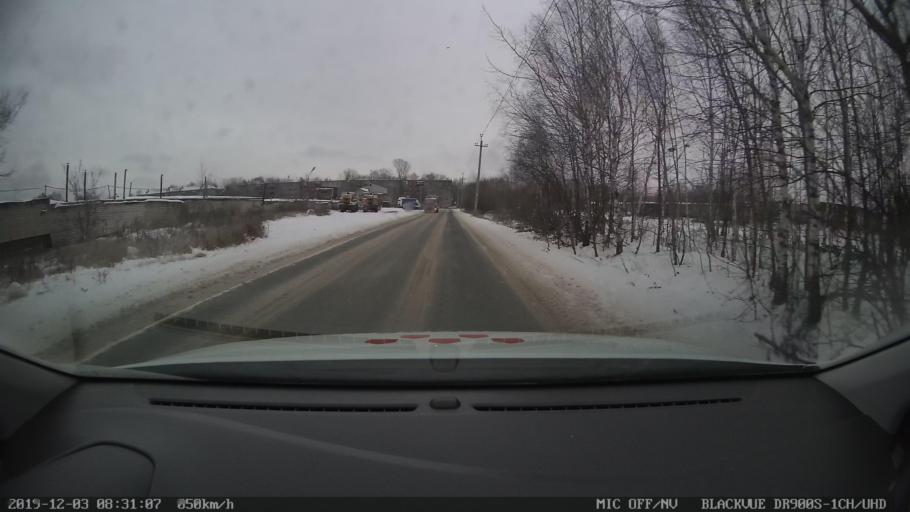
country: RU
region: Tatarstan
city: Staroye Arakchino
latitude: 55.8773
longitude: 49.0095
